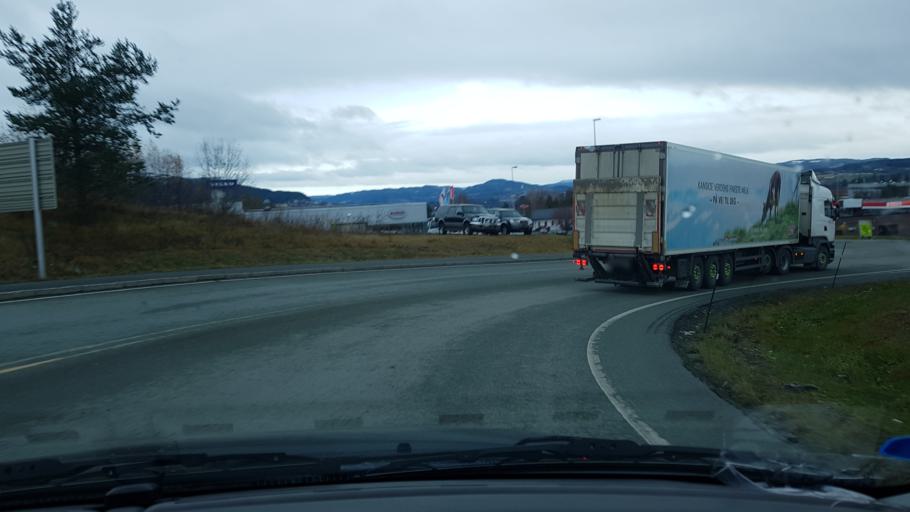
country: NO
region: Sor-Trondelag
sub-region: Melhus
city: Melhus
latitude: 63.3331
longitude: 10.3589
